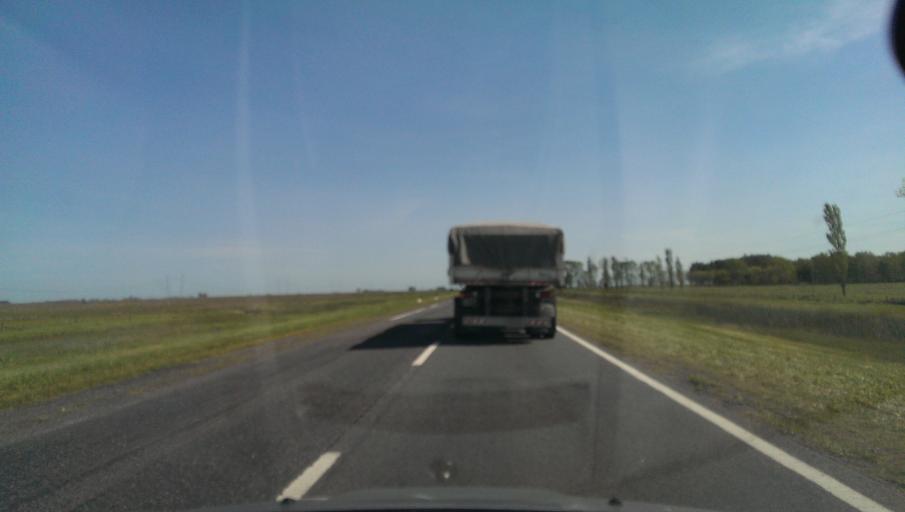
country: AR
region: Buenos Aires
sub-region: Partido de Azul
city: Azul
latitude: -36.6087
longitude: -59.6752
